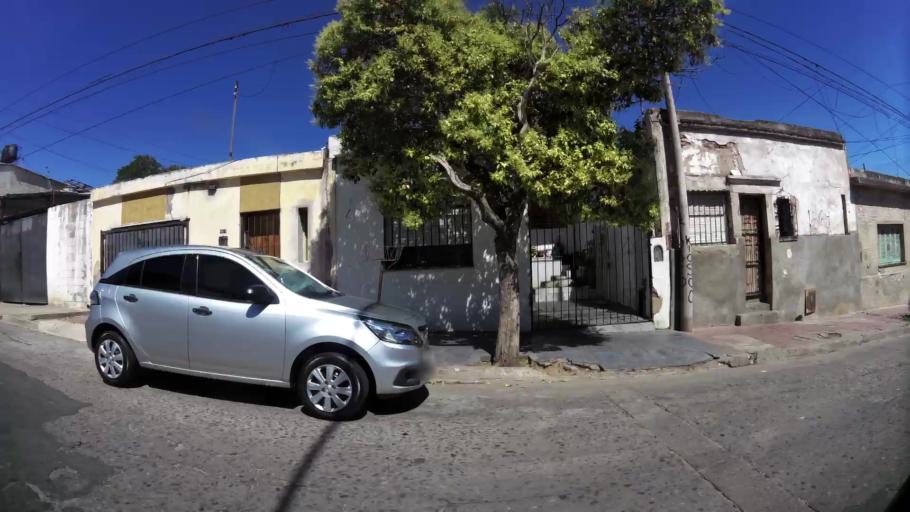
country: AR
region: Cordoba
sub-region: Departamento de Capital
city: Cordoba
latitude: -31.4263
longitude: -64.1586
